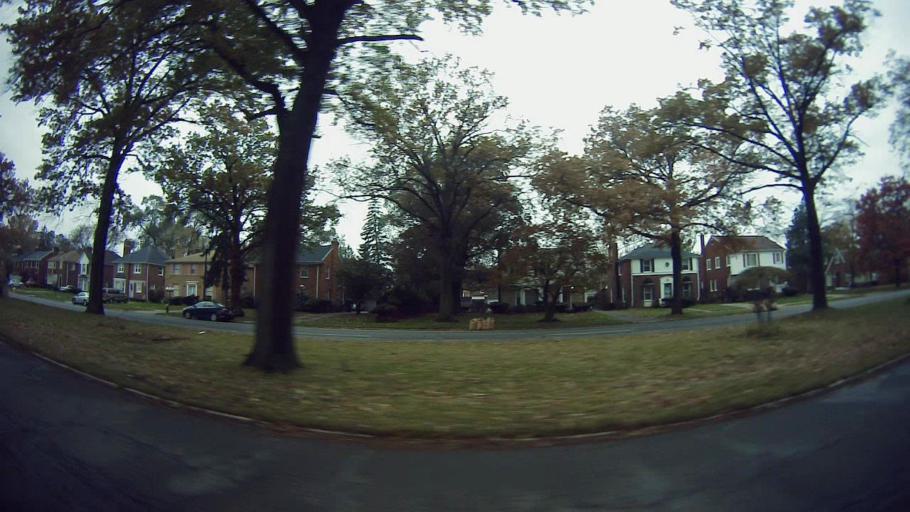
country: US
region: Michigan
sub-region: Oakland County
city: Oak Park
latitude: 42.4270
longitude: -83.1752
